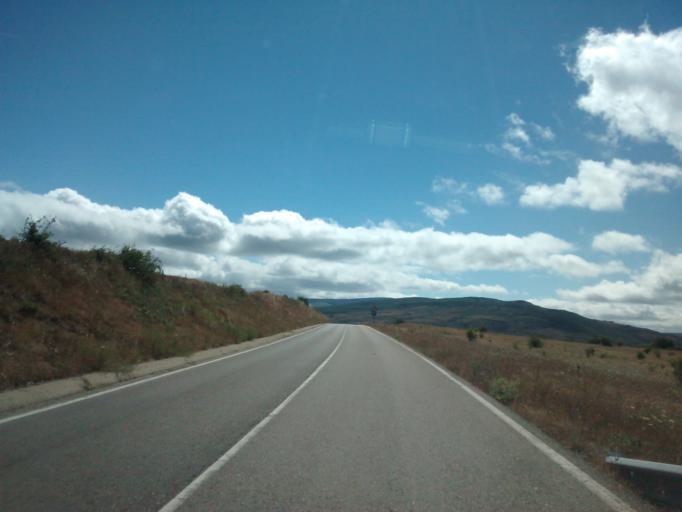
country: ES
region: Cantabria
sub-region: Provincia de Cantabria
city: Mataporquera
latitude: 42.9079
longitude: -4.1021
